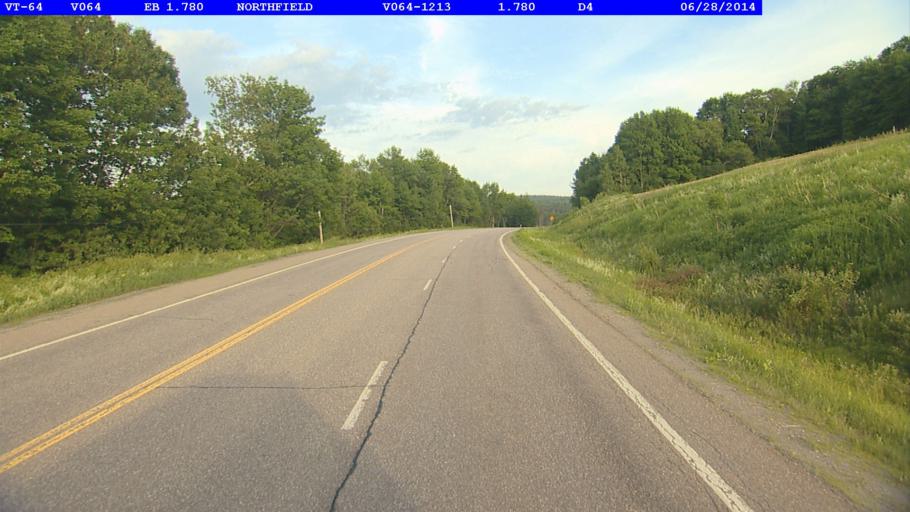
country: US
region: Vermont
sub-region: Washington County
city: Northfield
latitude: 44.1173
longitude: -72.6266
